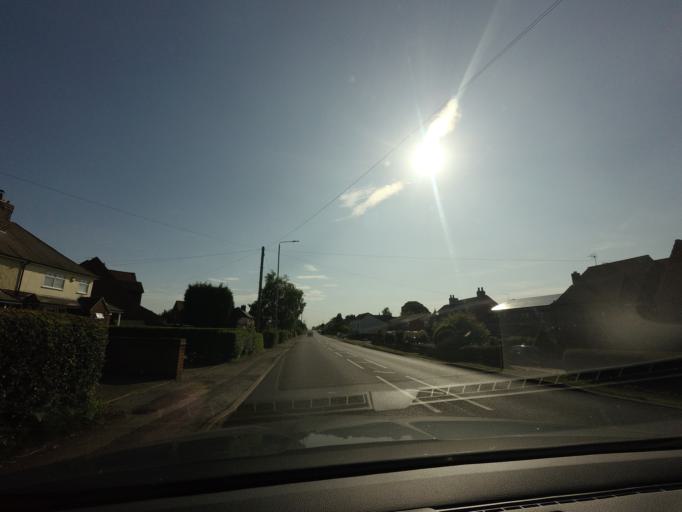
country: GB
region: England
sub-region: Derbyshire
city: Pinxton
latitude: 53.0539
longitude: -1.2892
